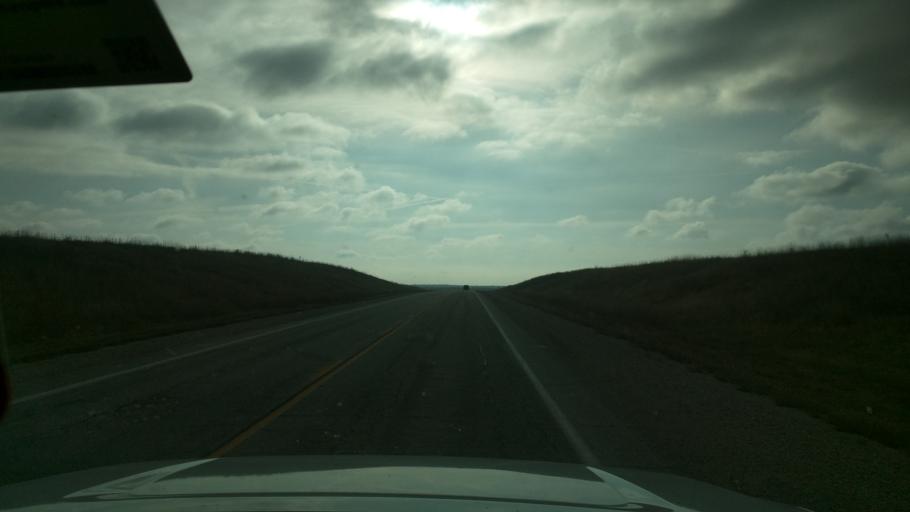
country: US
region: Kansas
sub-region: Chautauqua County
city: Sedan
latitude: 37.0951
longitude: -96.2300
